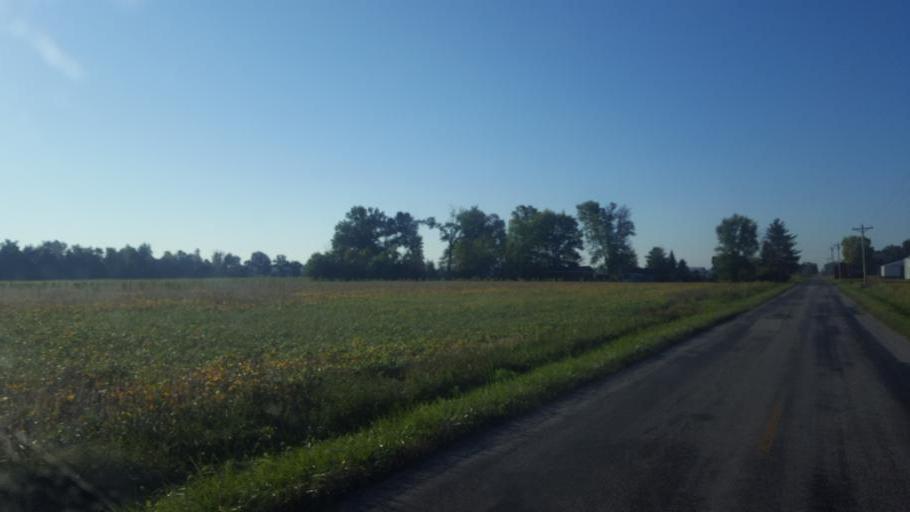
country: US
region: Ohio
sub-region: Morrow County
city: Cardington
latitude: 40.5463
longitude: -82.9956
